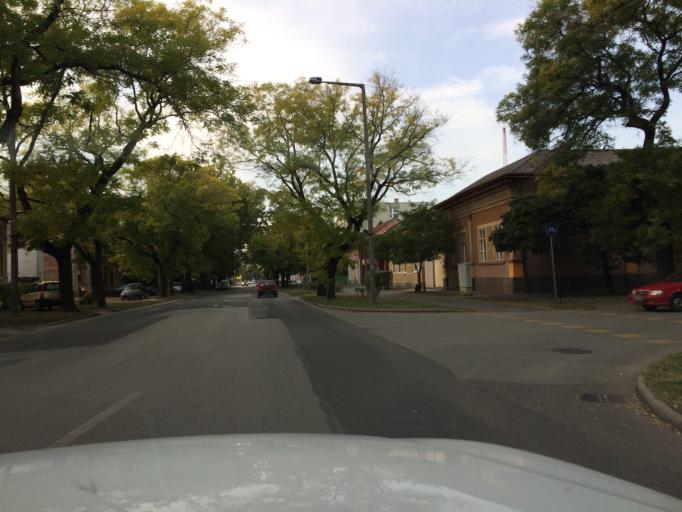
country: HU
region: Szabolcs-Szatmar-Bereg
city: Nyiregyhaza
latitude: 47.9556
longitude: 21.7079
